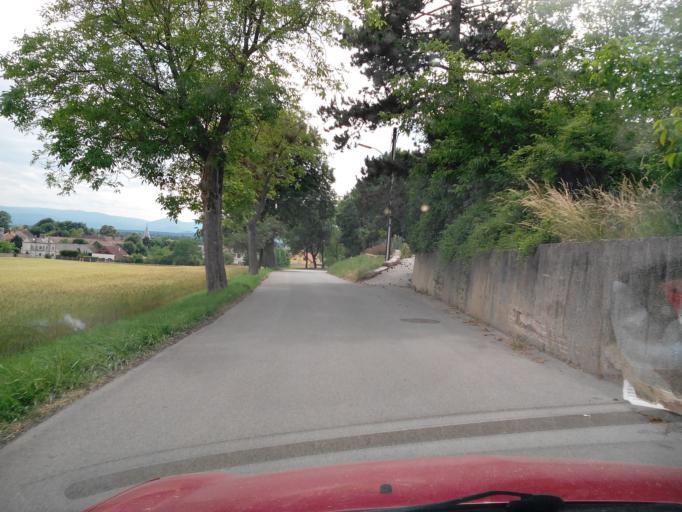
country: AT
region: Lower Austria
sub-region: Politischer Bezirk Wiener Neustadt
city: Weikersdorf am Steinfelde
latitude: 47.8307
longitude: 16.1575
